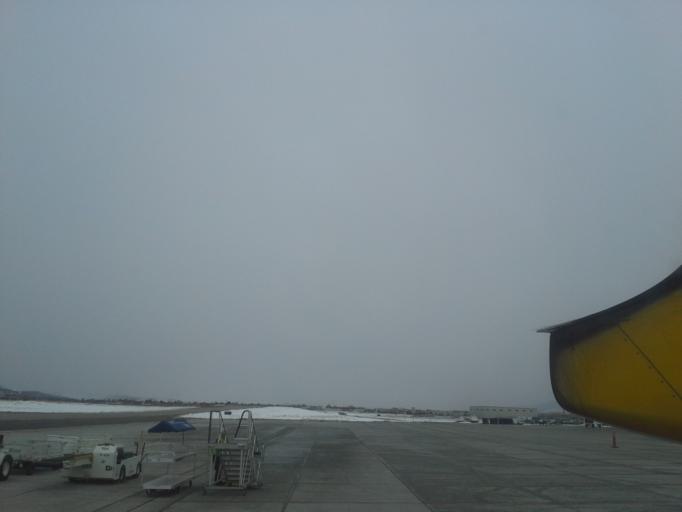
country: US
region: Montana
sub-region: Lewis and Clark County
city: Helena
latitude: 46.6060
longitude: -112.0025
